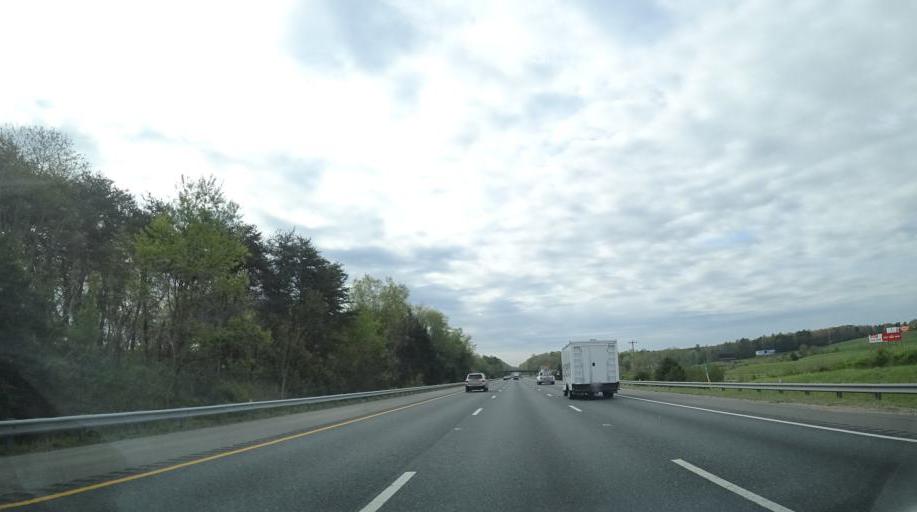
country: US
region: Virginia
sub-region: Spotsylvania County
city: Spotsylvania Courthouse
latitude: 38.0691
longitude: -77.5095
